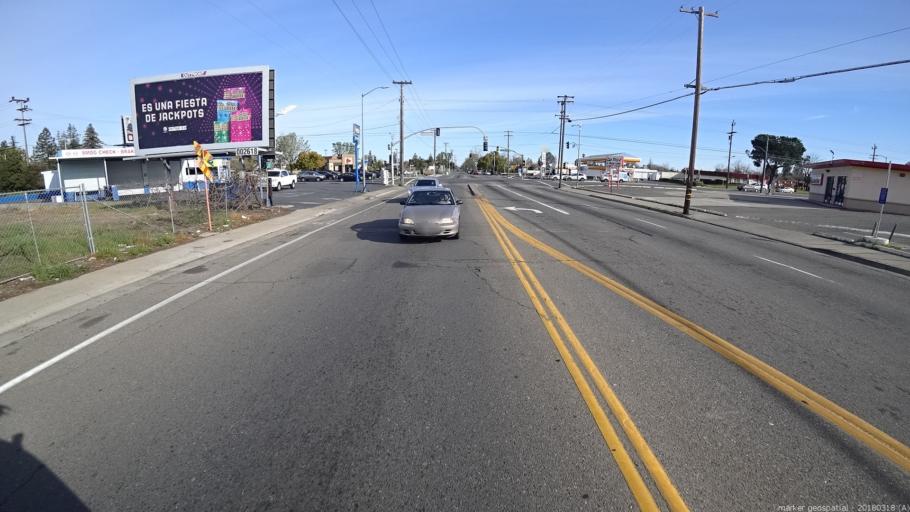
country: US
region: California
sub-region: Sacramento County
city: Parkway
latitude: 38.5245
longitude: -121.4647
